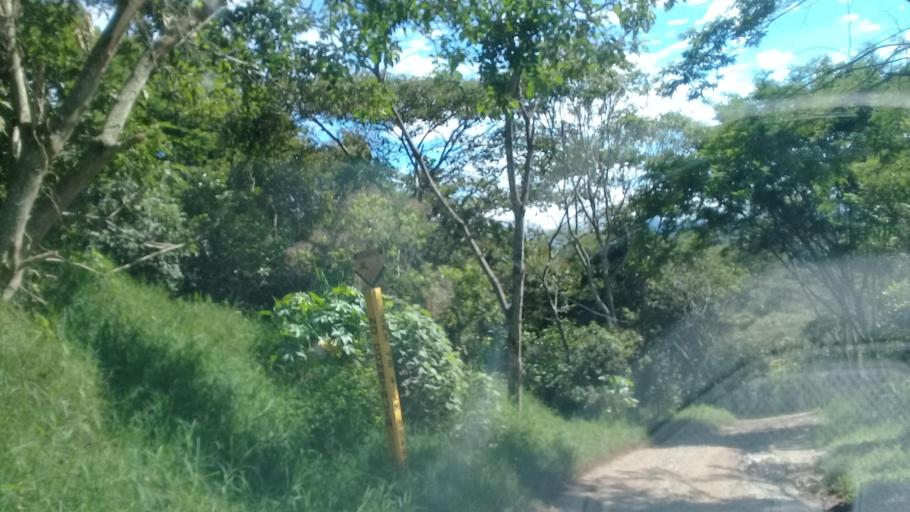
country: MX
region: Veracruz
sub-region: Jilotepec
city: El Pueblito (Garbanzal)
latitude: 19.5782
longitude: -96.9008
